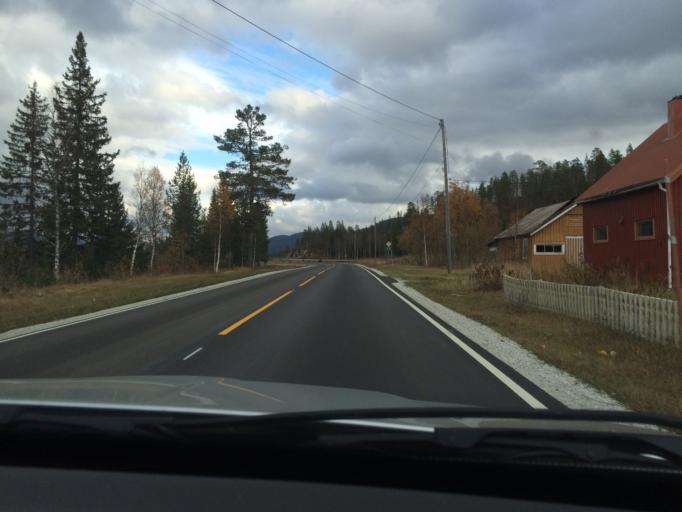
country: NO
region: Nord-Trondelag
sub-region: Namsskogan
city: Namsskogan
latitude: 64.7771
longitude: 12.8847
